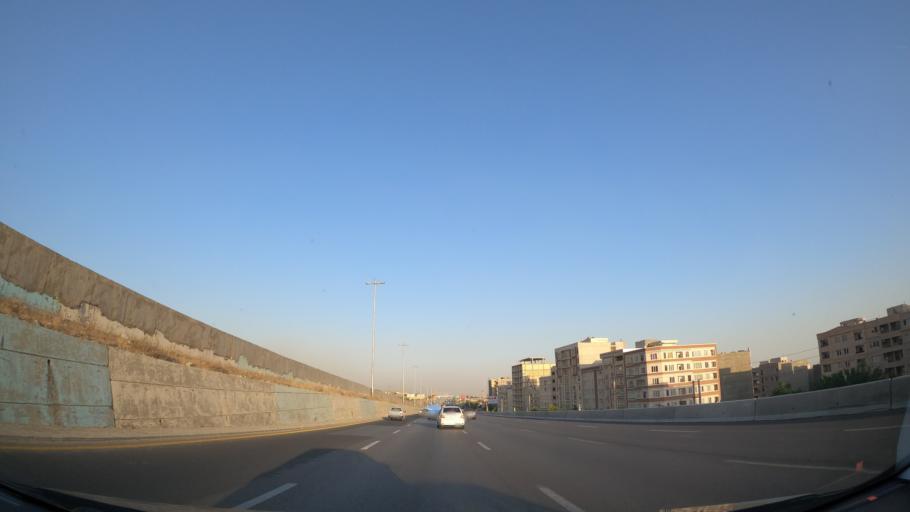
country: IR
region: Tehran
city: Shahr-e Qods
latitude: 35.7578
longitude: 51.0688
